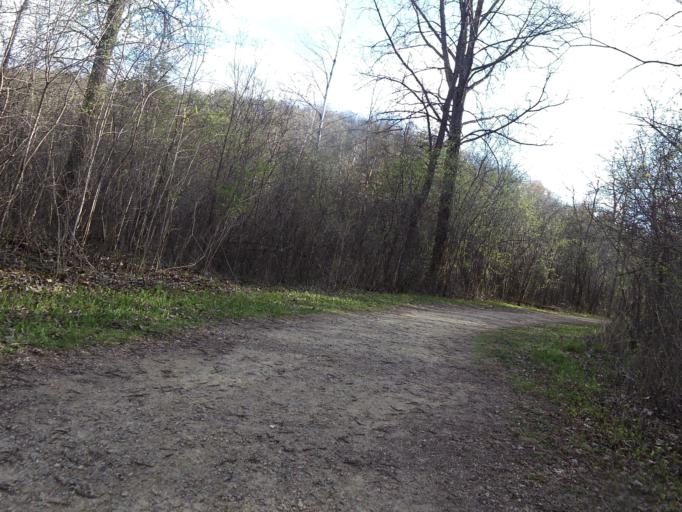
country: US
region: Wisconsin
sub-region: Saint Croix County
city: North Hudson
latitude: 45.0183
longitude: -92.6841
